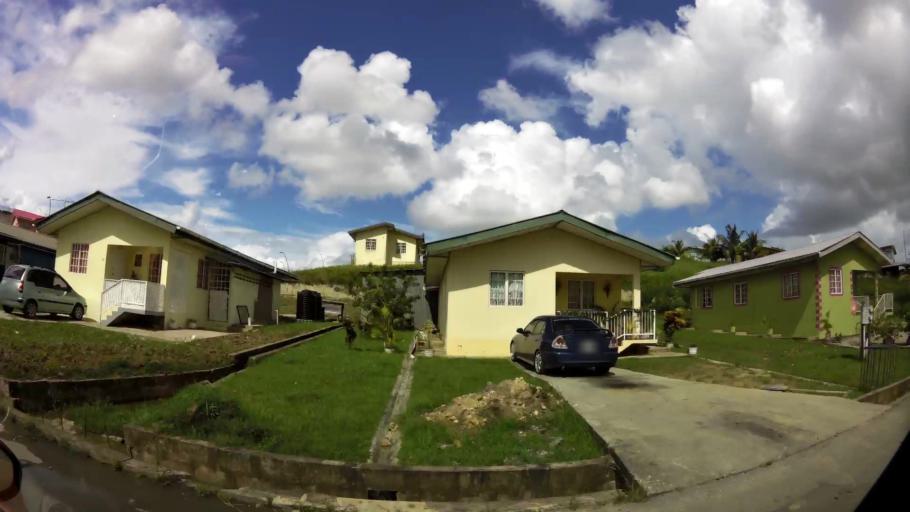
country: TT
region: Penal/Debe
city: Debe
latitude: 10.2410
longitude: -61.4389
